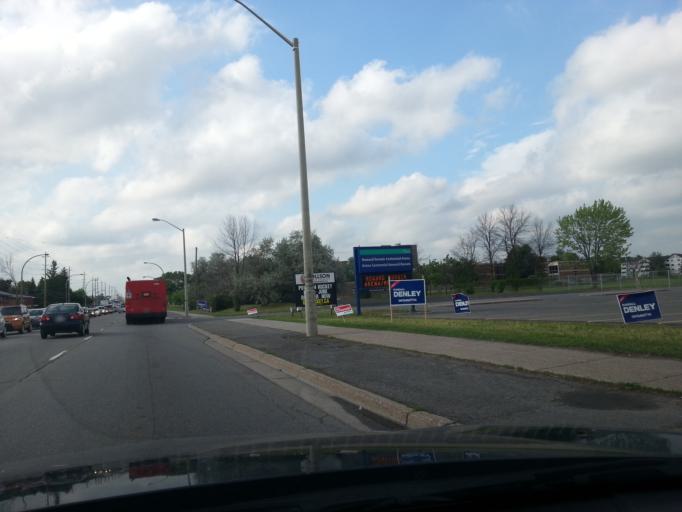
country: CA
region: Ontario
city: Ottawa
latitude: 45.3412
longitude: -75.7278
